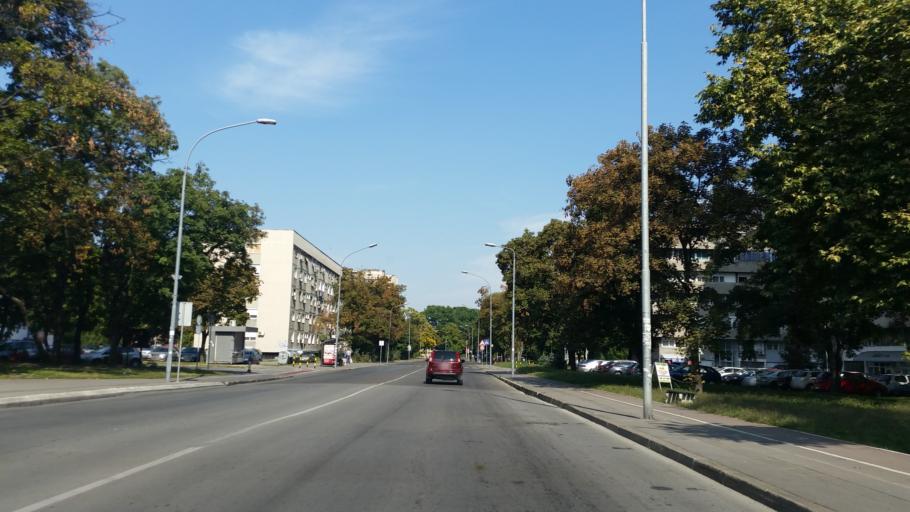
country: RS
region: Central Serbia
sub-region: Belgrade
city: Zemun
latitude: 44.8256
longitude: 20.4021
